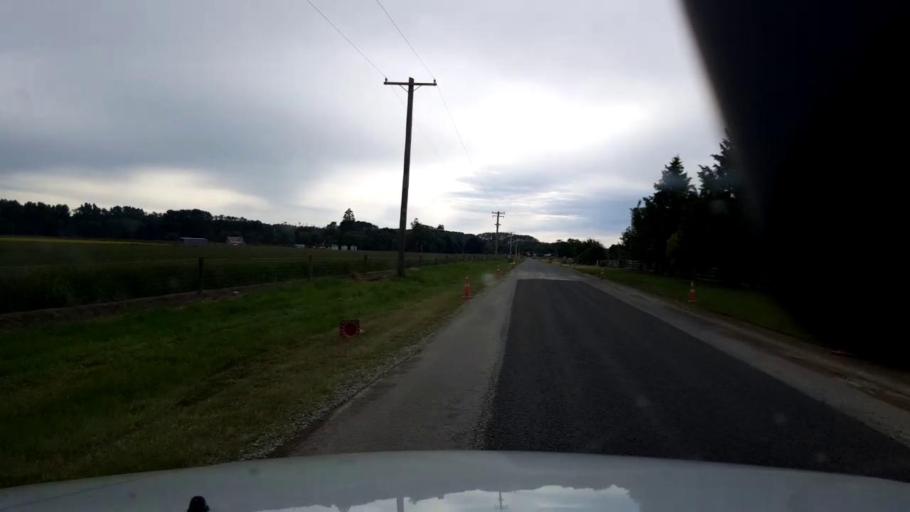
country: NZ
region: Canterbury
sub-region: Timaru District
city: Pleasant Point
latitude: -44.2706
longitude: 171.2579
